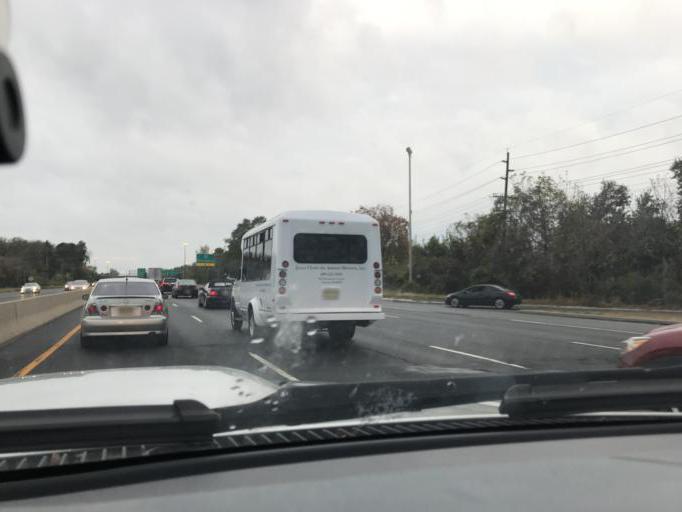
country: US
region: New Jersey
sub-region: Mercer County
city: Princeton
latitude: 40.3020
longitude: -74.6737
